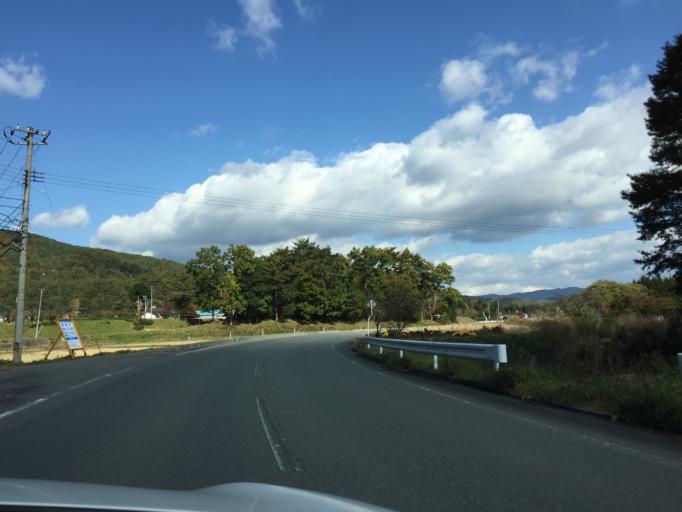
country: JP
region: Fukushima
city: Funehikimachi-funehiki
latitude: 37.3213
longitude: 140.7821
